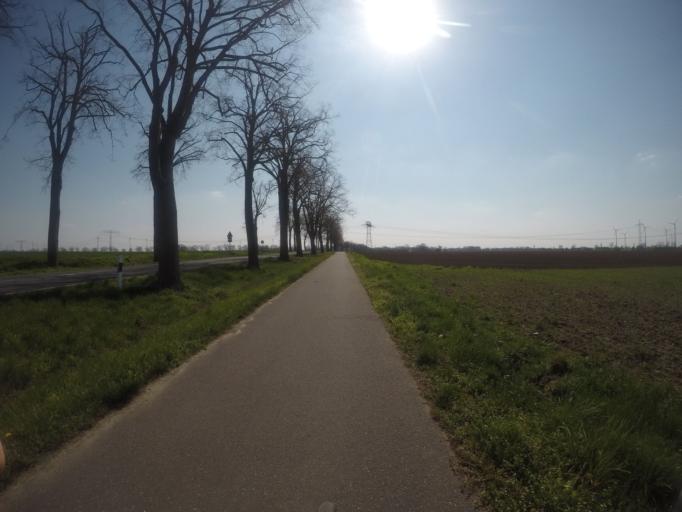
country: DE
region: Brandenburg
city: Nauen
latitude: 52.5888
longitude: 12.8763
